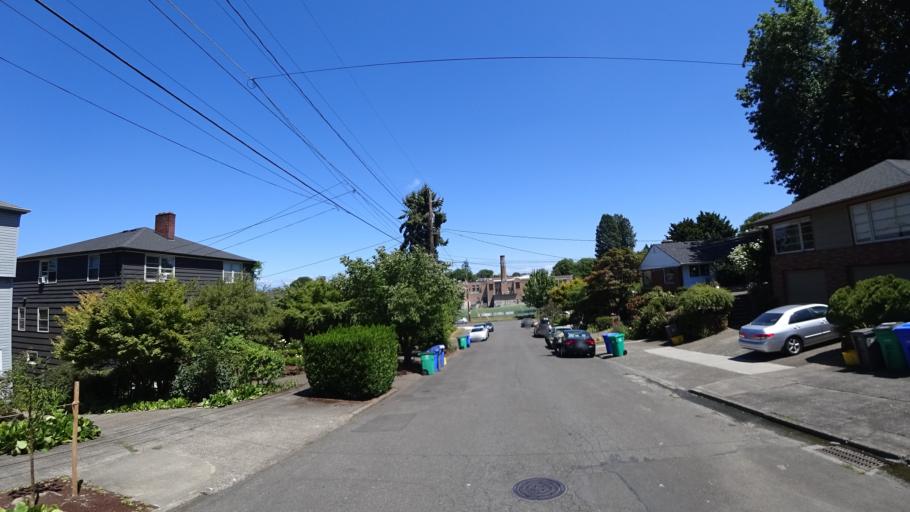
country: US
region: Oregon
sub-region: Multnomah County
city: Portland
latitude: 45.5332
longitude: -122.7078
